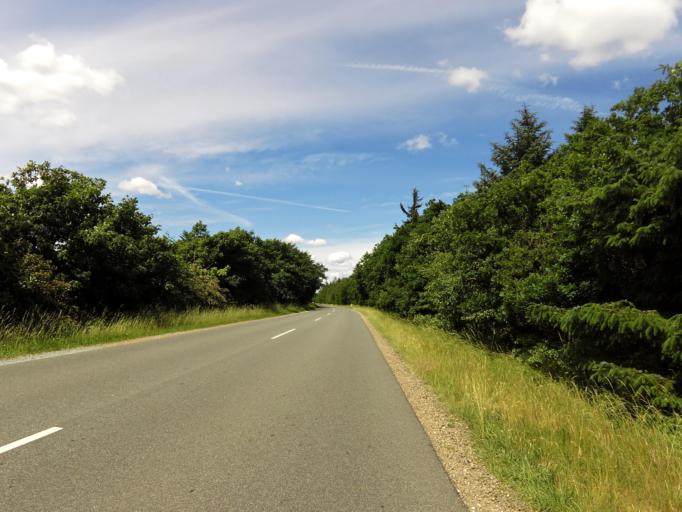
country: DK
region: South Denmark
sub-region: Esbjerg Kommune
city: Ribe
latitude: 55.2886
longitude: 8.7817
